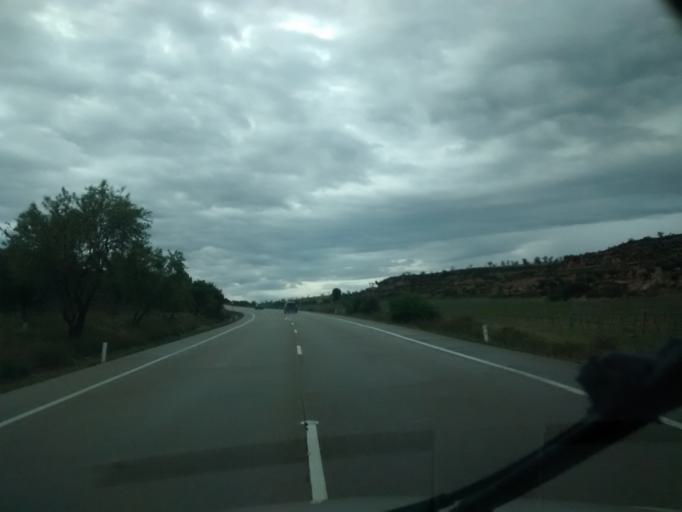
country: ES
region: Aragon
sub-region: Provincia de Zaragoza
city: Maella
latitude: 41.1390
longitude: 0.1210
